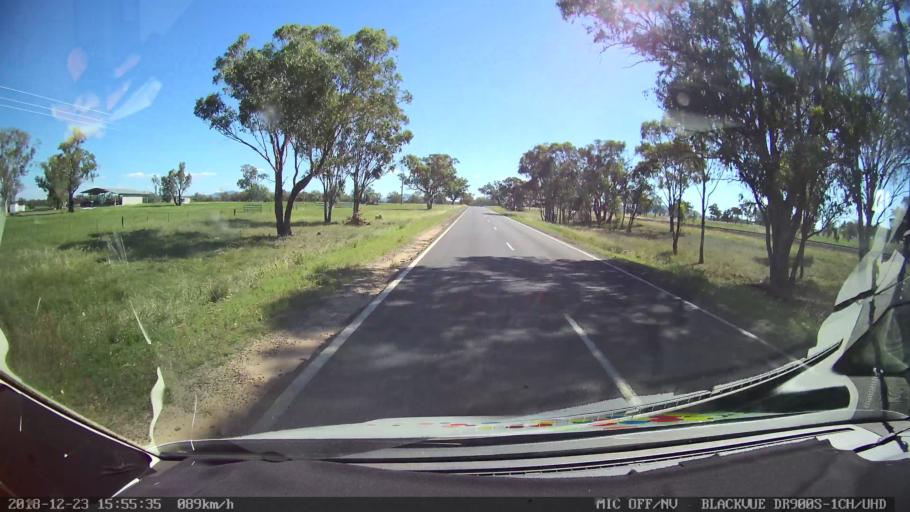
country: AU
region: New South Wales
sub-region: Tamworth Municipality
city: Phillip
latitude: -31.1570
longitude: 150.8668
